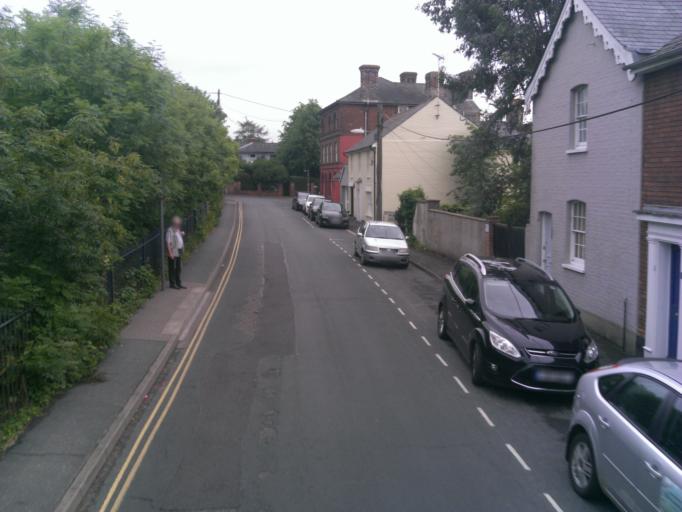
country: GB
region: England
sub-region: Essex
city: Wivenhoe
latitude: 51.8560
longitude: 0.9581
